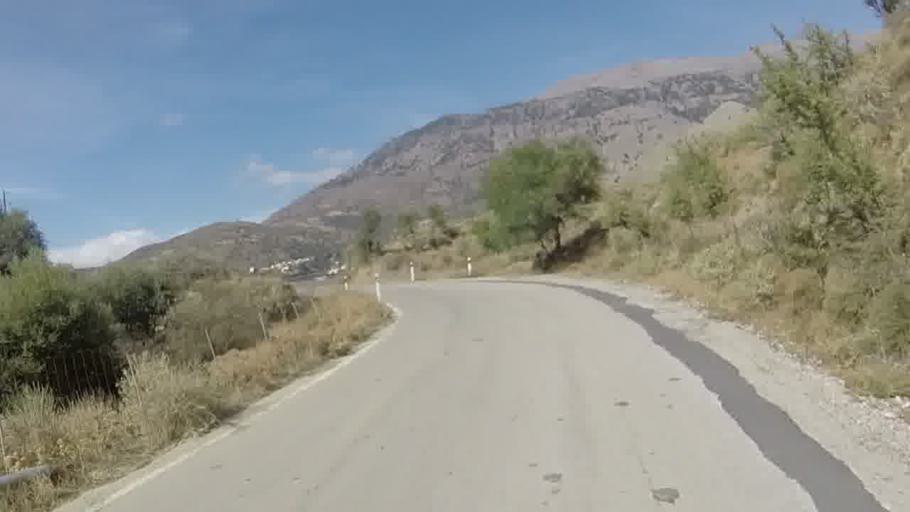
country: GR
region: Crete
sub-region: Nomos Rethymnis
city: Agia Galini
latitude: 35.1788
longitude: 24.7379
